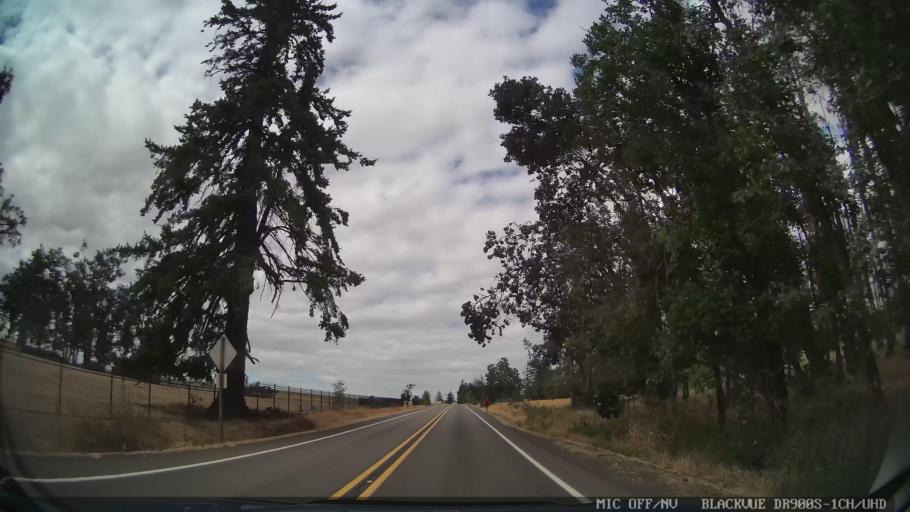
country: US
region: Oregon
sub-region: Marion County
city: Sublimity
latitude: 44.8525
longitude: -122.7933
